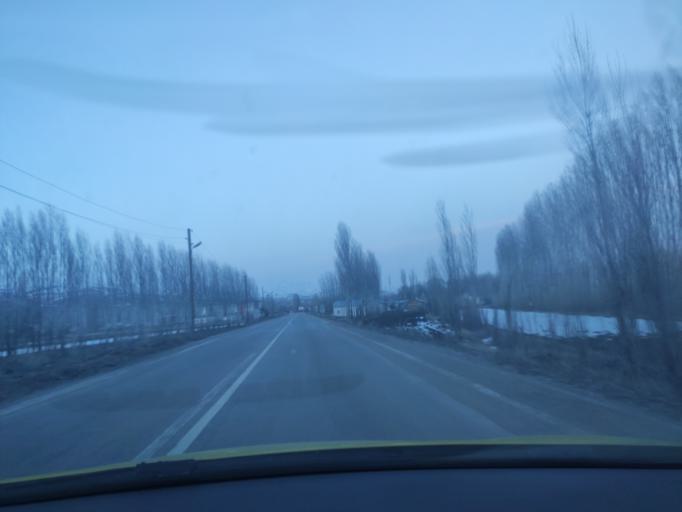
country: TR
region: Bayburt
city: Aydintepe
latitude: 40.3604
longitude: 40.1018
